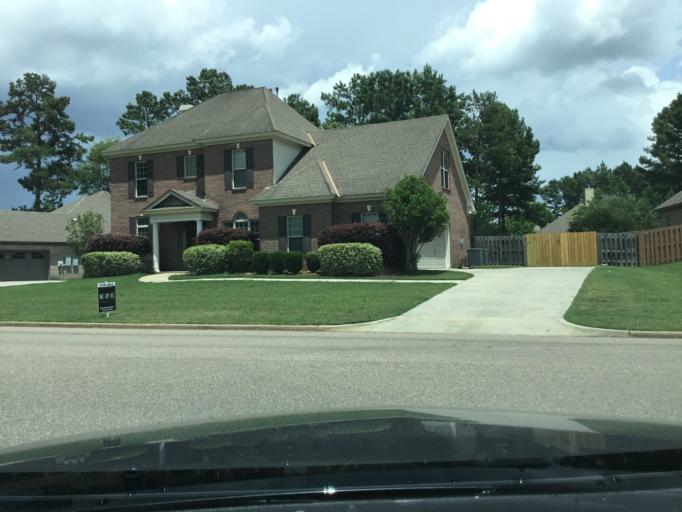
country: US
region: Alabama
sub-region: Montgomery County
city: Pike Road
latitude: 32.3424
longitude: -86.0839
